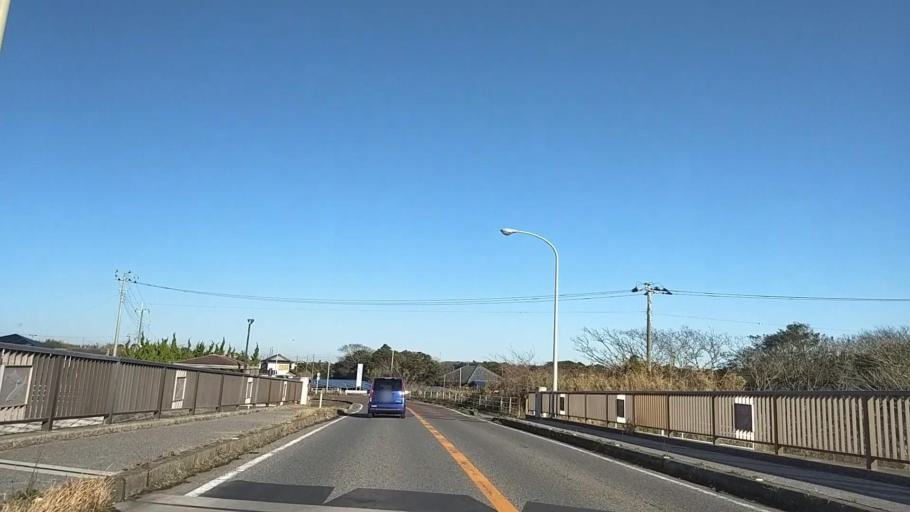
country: JP
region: Chiba
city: Yokaichiba
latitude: 35.6155
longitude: 140.5320
